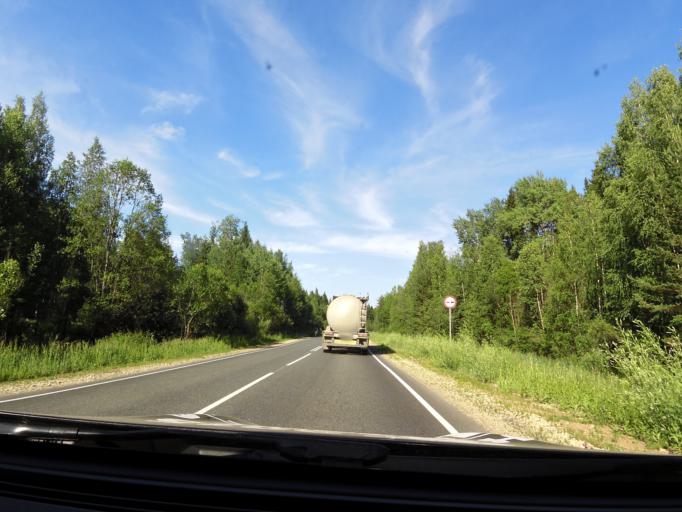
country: RU
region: Kirov
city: Belaya Kholunitsa
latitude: 58.9035
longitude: 50.9394
